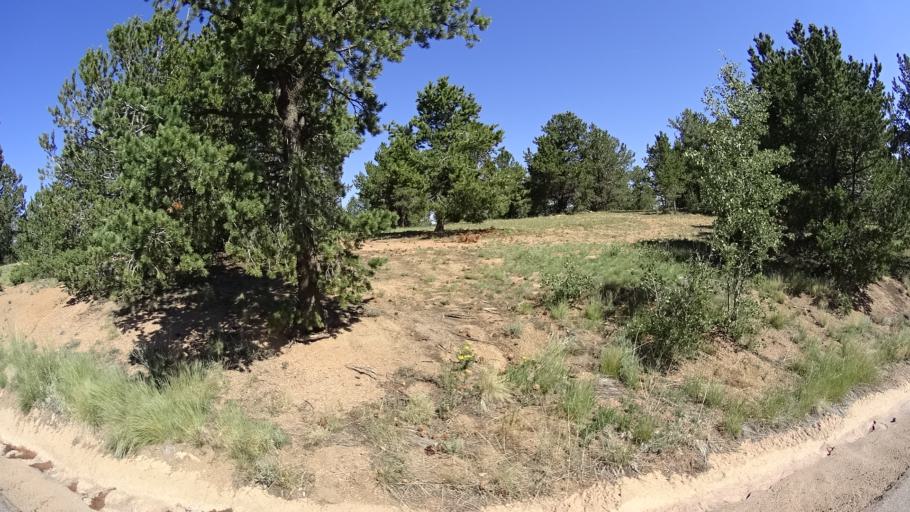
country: US
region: Colorado
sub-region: El Paso County
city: Cascade-Chipita Park
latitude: 38.9052
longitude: -105.0576
